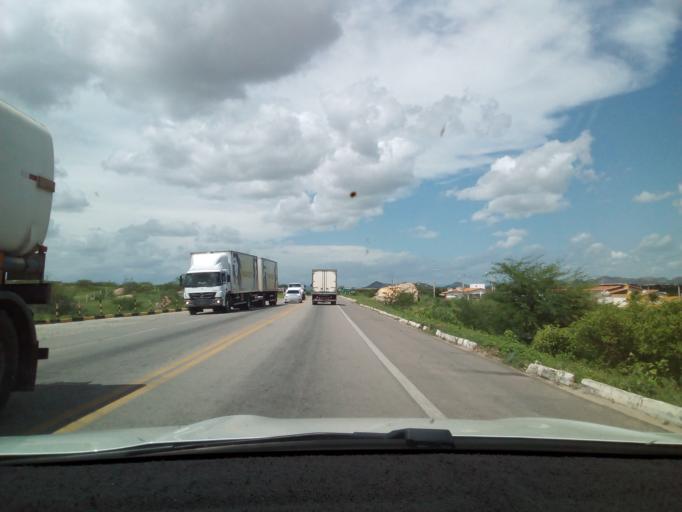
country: BR
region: Rio Grande do Norte
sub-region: Angicos
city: Angicos
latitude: -5.6945
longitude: -36.5283
